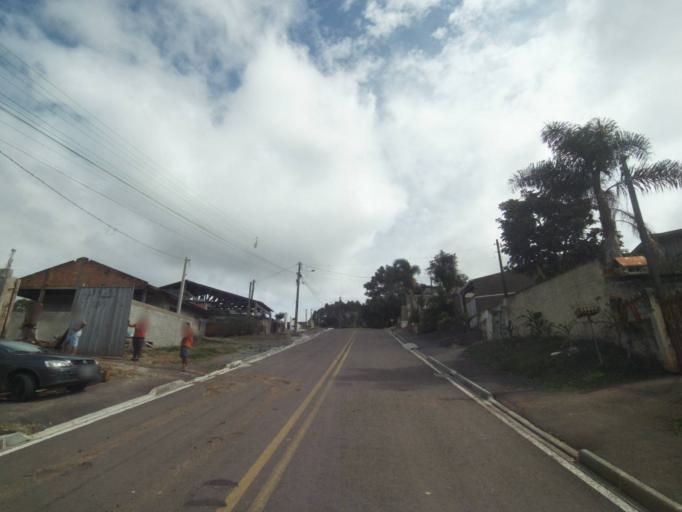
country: BR
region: Parana
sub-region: Quatro Barras
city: Quatro Barras
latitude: -25.3454
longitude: -49.0805
